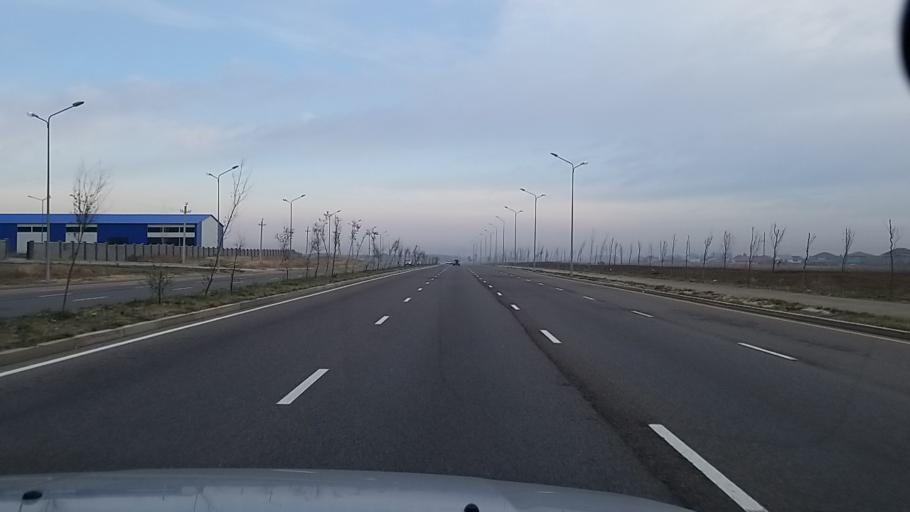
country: KZ
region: Almaty Oblysy
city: Burunday
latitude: 43.3387
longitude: 76.8335
